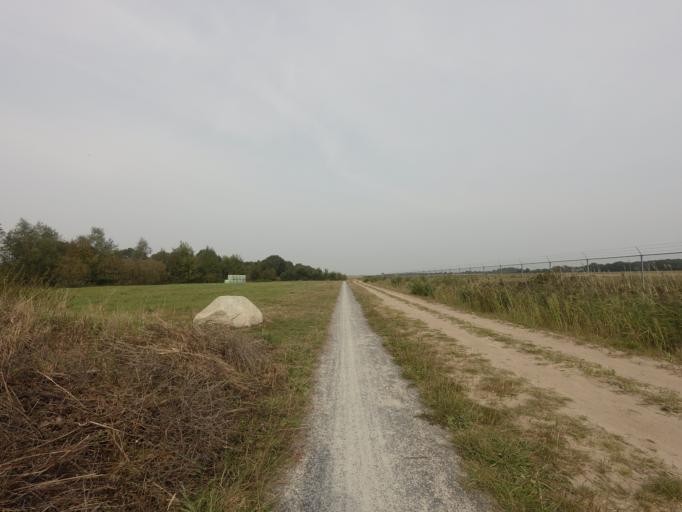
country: NL
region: Drenthe
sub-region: Gemeente Tynaarlo
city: Vries
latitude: 53.1147
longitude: 6.5641
